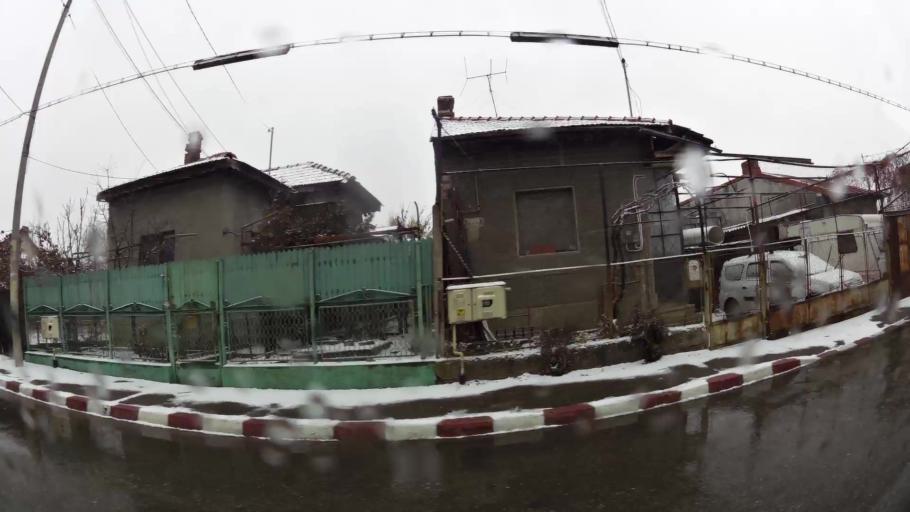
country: RO
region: Dambovita
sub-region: Municipiul Targoviste
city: Targoviste
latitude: 44.9265
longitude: 25.4699
